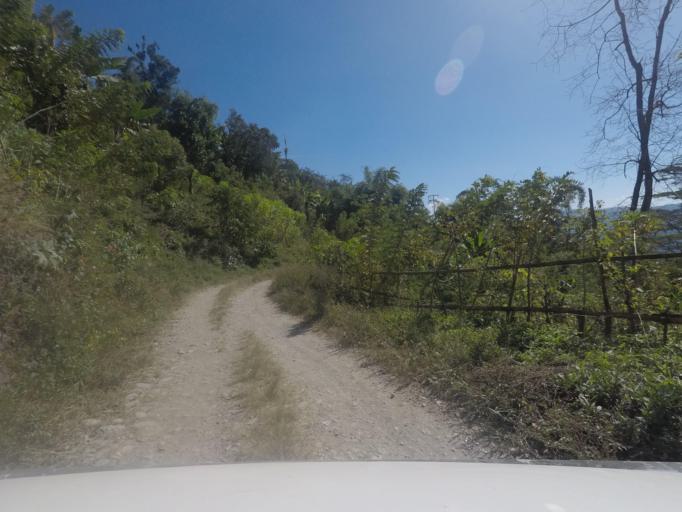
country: TL
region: Ermera
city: Gleno
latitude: -8.7260
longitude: 125.3323
